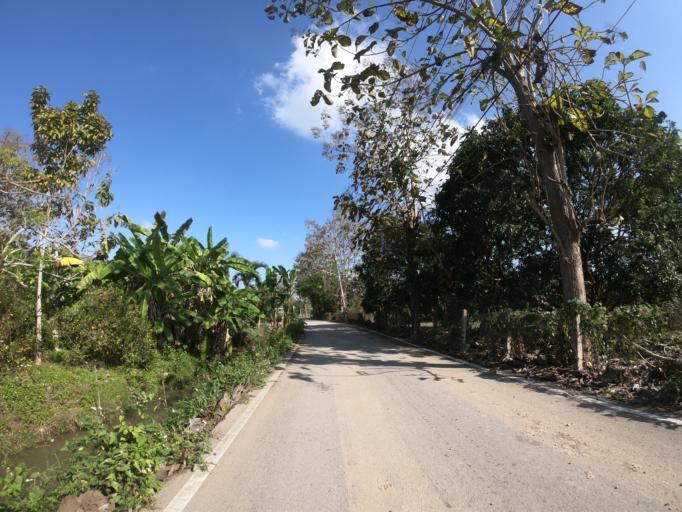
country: TH
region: Chiang Mai
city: Saraphi
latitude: 18.7140
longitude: 99.0132
